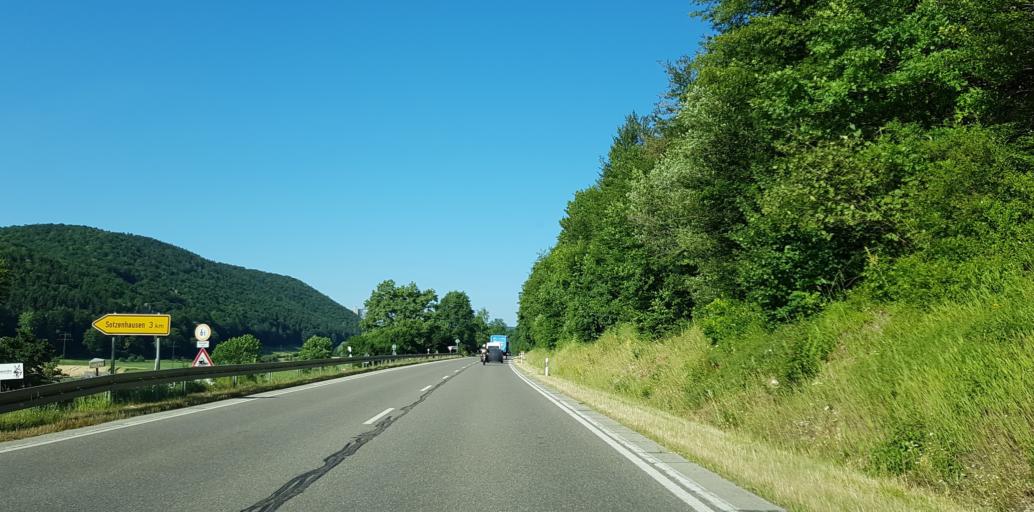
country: DE
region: Baden-Wuerttemberg
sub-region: Tuebingen Region
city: Schelklingen
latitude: 48.3861
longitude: 9.7605
